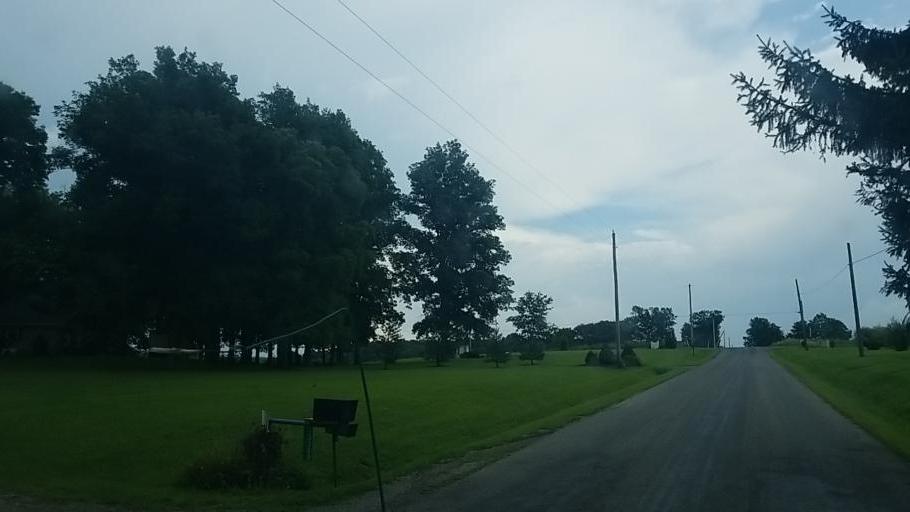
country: US
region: Ohio
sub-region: Wayne County
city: Creston
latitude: 40.9607
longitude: -81.9378
